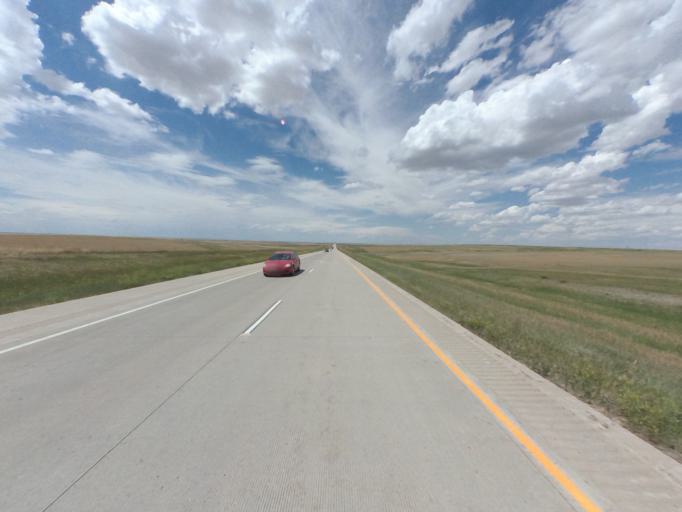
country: US
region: Colorado
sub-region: Lincoln County
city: Limon
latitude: 39.3949
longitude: -103.8961
